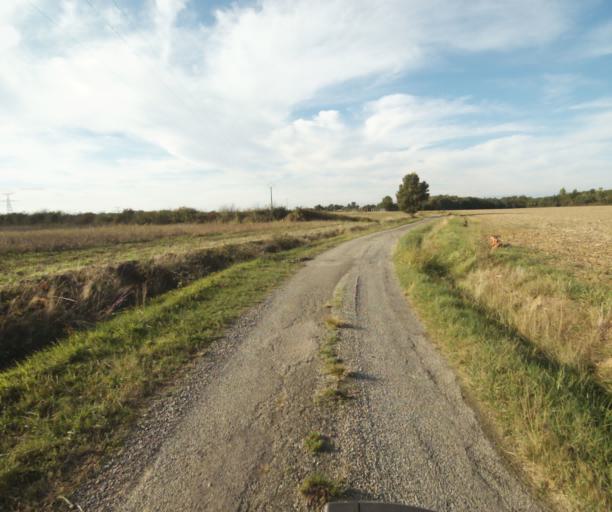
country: FR
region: Midi-Pyrenees
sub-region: Departement du Tarn-et-Garonne
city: Finhan
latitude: 43.9082
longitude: 1.1115
